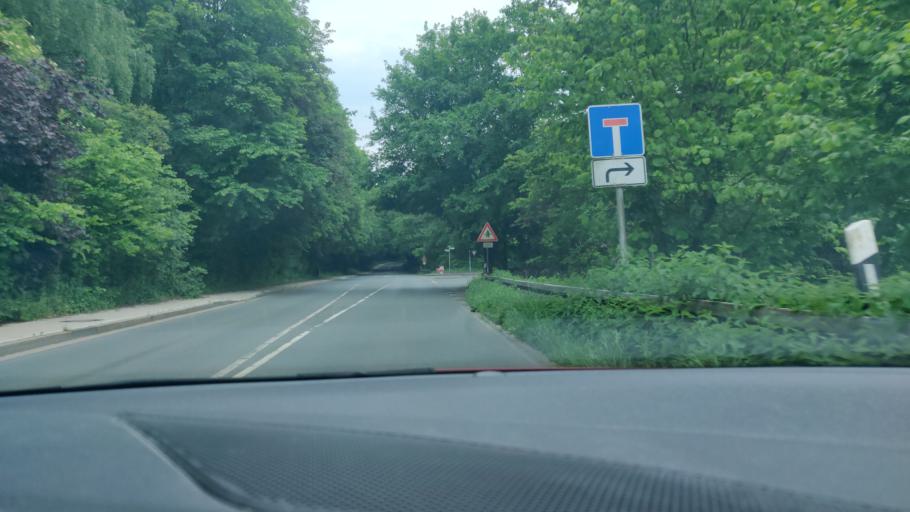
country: DE
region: North Rhine-Westphalia
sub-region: Regierungsbezirk Dusseldorf
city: Velbert
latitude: 51.3451
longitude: 7.0753
